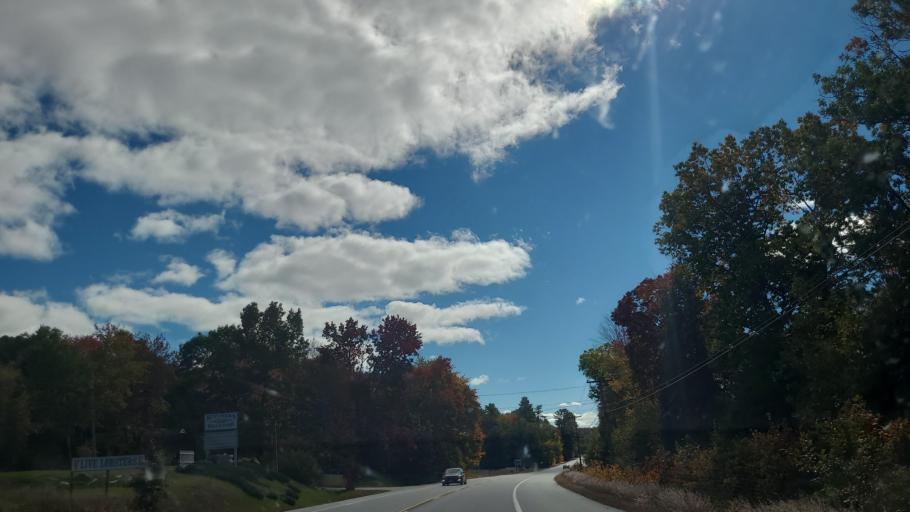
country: US
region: Maine
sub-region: Cumberland County
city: Raymond
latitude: 43.9408
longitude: -70.5449
